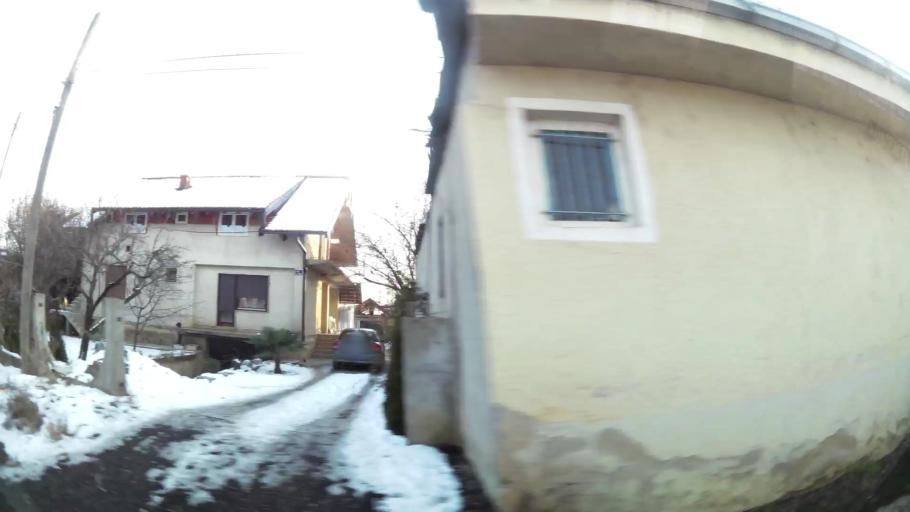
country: MK
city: Creshevo
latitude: 42.0276
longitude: 21.5213
